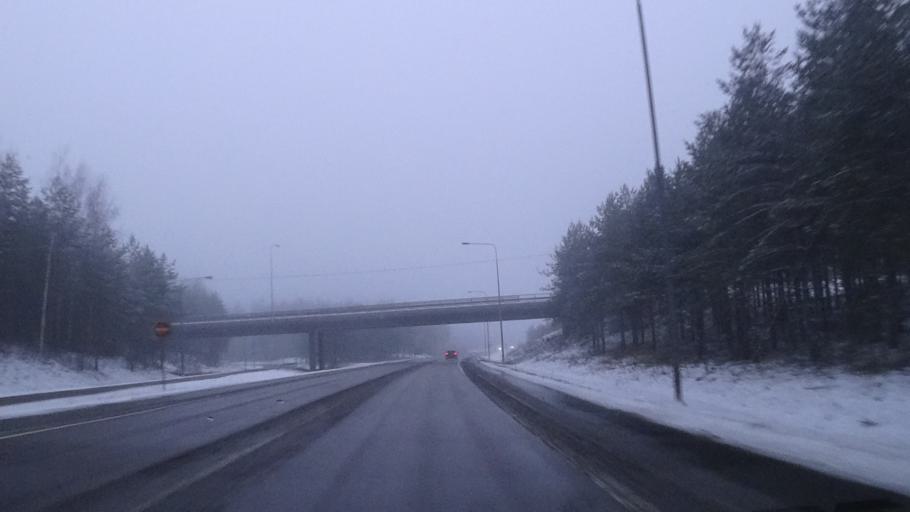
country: FI
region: Paijanne Tavastia
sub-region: Lahti
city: Hollola
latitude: 60.9831
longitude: 25.4225
